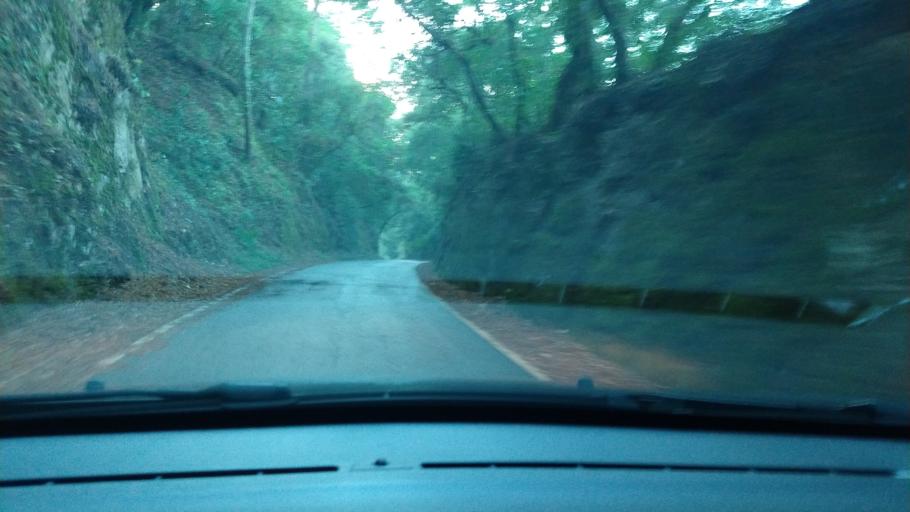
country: PT
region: Lisbon
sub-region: Sintra
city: Colares
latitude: 38.7919
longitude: -9.4218
